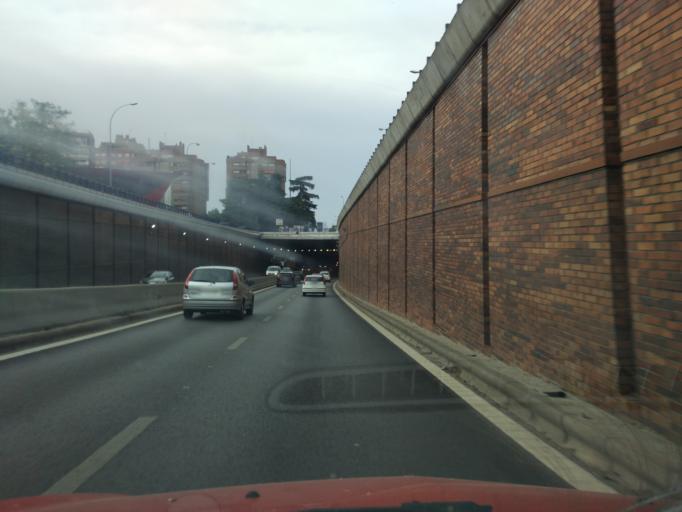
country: ES
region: Madrid
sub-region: Provincia de Madrid
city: Carabanchel
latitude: 40.3837
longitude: -3.7180
